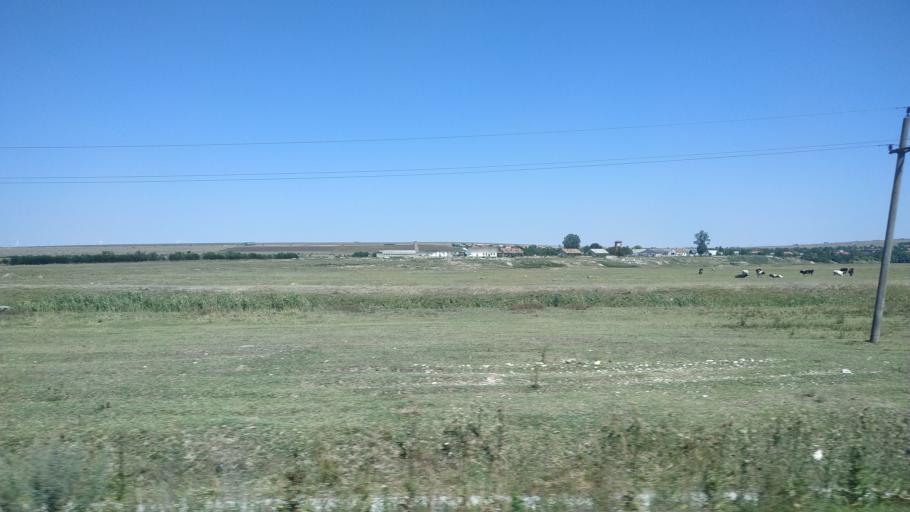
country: RO
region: Constanta
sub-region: Comuna Mircea Voda
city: Satu Nou
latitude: 44.2597
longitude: 28.2138
